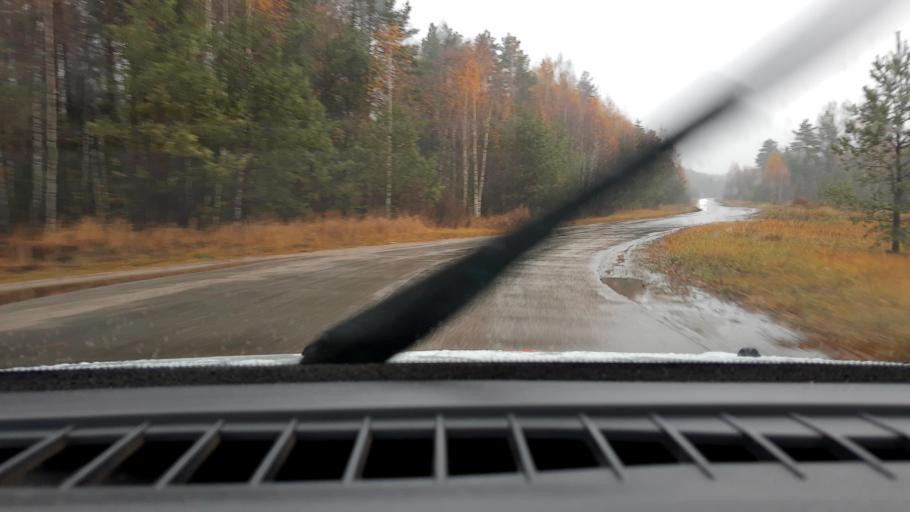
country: RU
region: Nizjnij Novgorod
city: Linda
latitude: 56.6925
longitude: 44.2033
